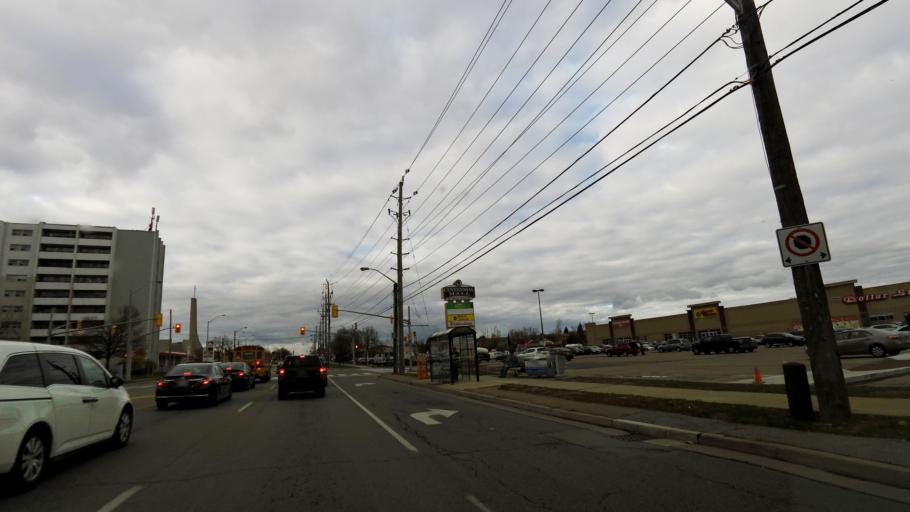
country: CA
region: Ontario
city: Brampton
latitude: 43.7014
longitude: -79.7570
